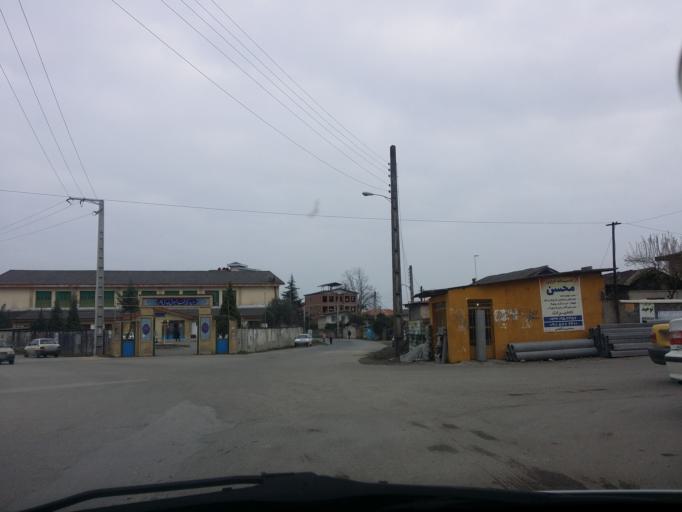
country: IR
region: Mazandaran
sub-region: Nowshahr
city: Nowshahr
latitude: 36.6441
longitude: 51.4808
